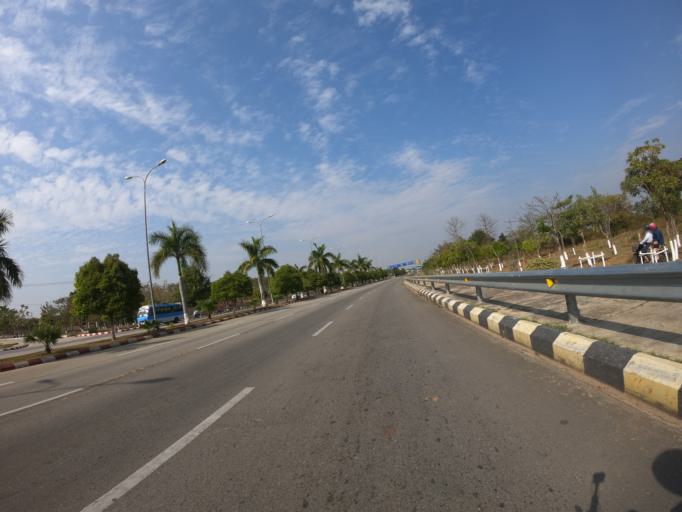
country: MM
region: Mandalay
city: Nay Pyi Taw
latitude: 19.6684
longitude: 96.1210
